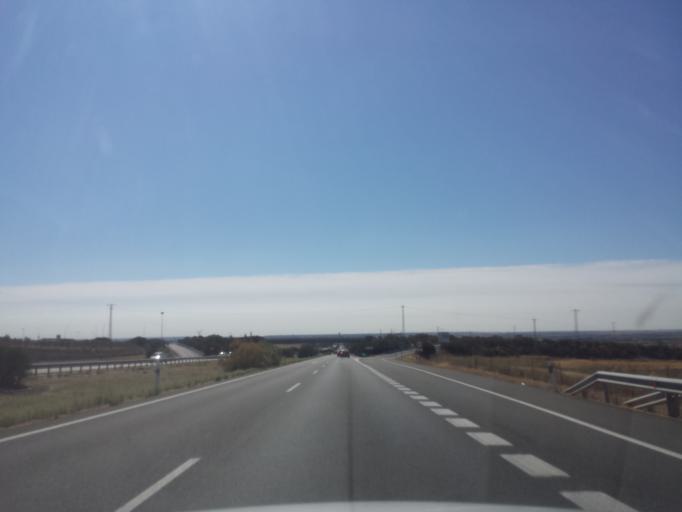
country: ES
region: Castille and Leon
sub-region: Provincia de Valladolid
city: Bercero
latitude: 41.5263
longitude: -5.0463
